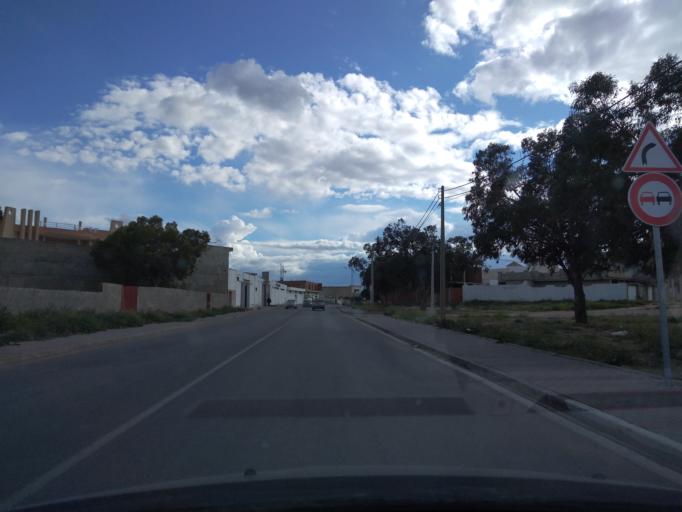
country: TN
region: Susah
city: Masakin
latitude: 35.7177
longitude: 10.5642
